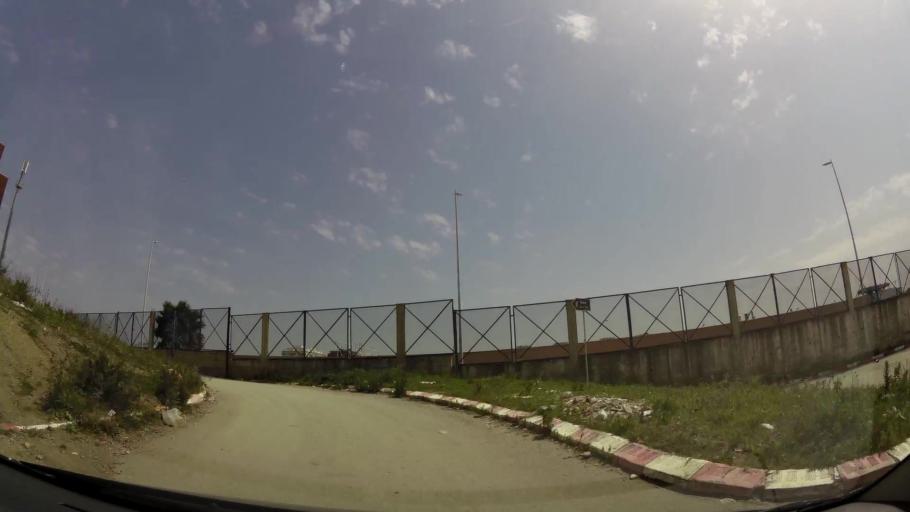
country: MA
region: Tanger-Tetouan
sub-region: Tanger-Assilah
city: Tangier
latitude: 35.7466
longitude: -5.8459
